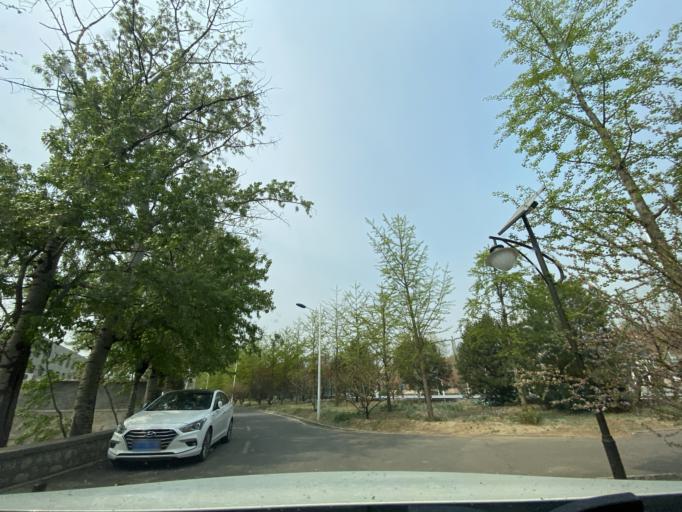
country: CN
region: Beijing
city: Sijiqing
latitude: 39.9402
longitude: 116.2473
